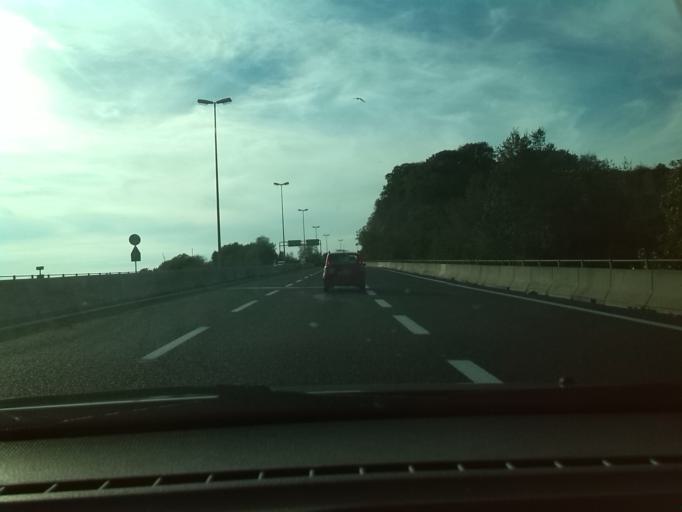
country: IT
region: Friuli Venezia Giulia
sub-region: Provincia di Trieste
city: Trieste
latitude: 45.6144
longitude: 13.7994
